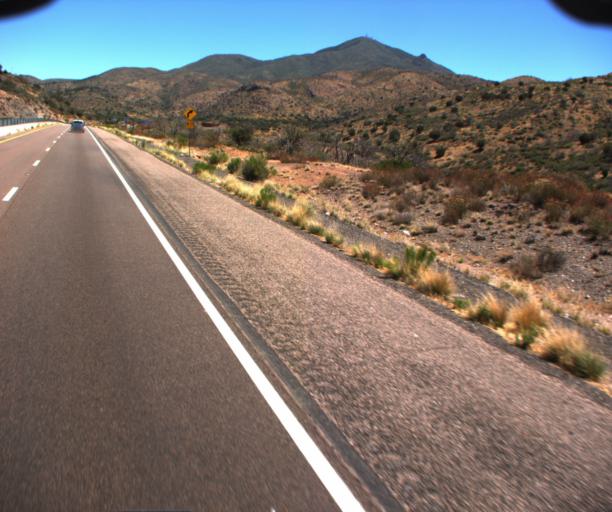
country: US
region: Arizona
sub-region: Gila County
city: Tonto Basin
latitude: 33.8746
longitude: -111.4610
